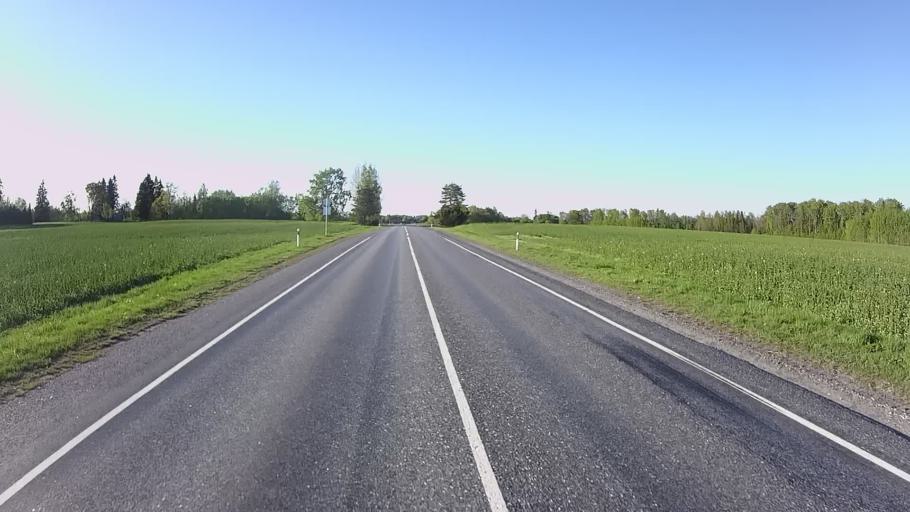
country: EE
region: Viljandimaa
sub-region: Vohma linn
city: Vohma
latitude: 58.5188
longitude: 25.5859
